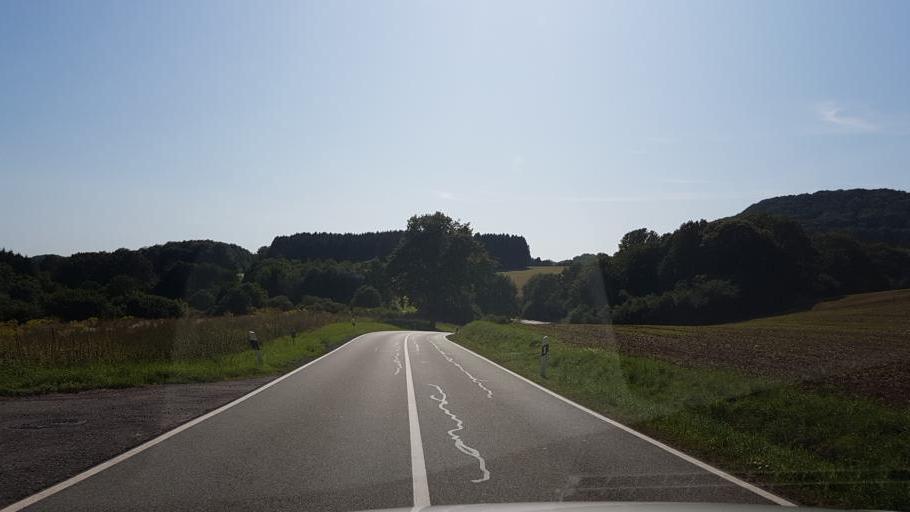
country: DE
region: Saarland
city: Tholey
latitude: 49.5052
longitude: 7.0027
